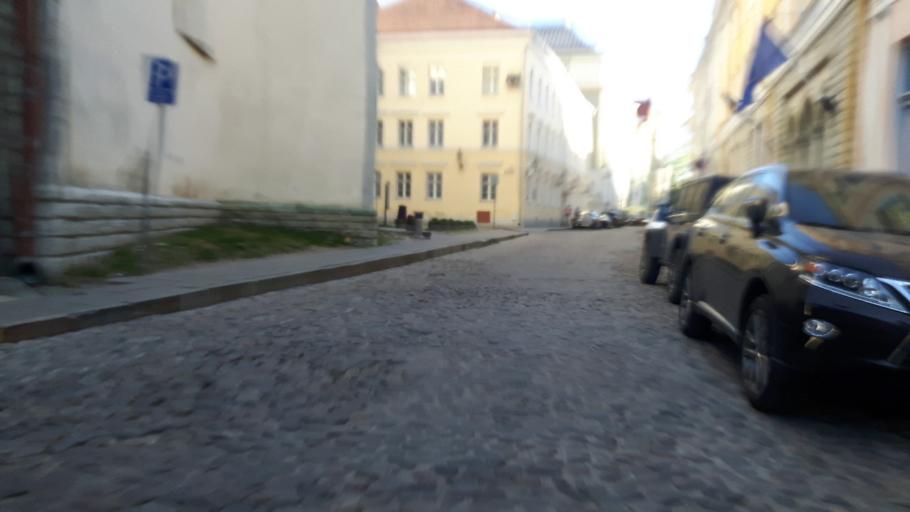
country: EE
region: Harju
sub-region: Tallinna linn
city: Tallinn
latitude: 59.4416
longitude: 24.7474
